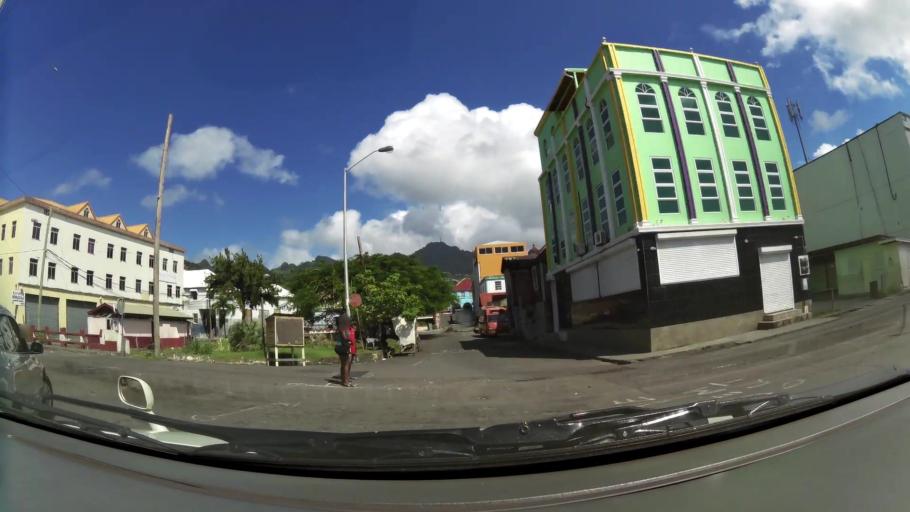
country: VC
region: Saint George
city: Kingstown Park
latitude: 13.1564
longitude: -61.2299
